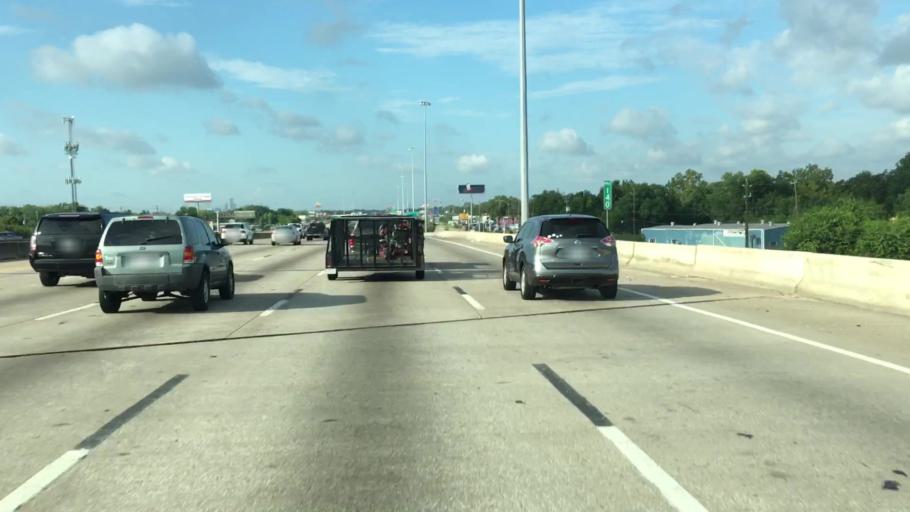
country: US
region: Texas
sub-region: Harris County
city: Aldine
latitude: 29.8798
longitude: -95.3263
